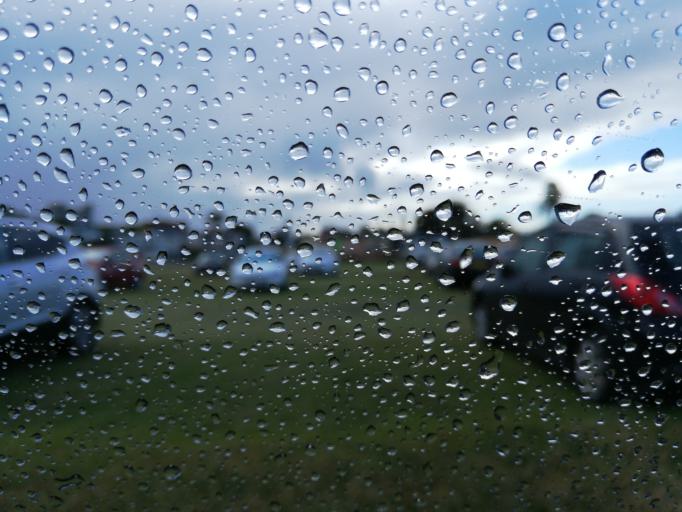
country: MU
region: Plaines Wilhems
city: Ebene
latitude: -20.2543
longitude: 57.4887
